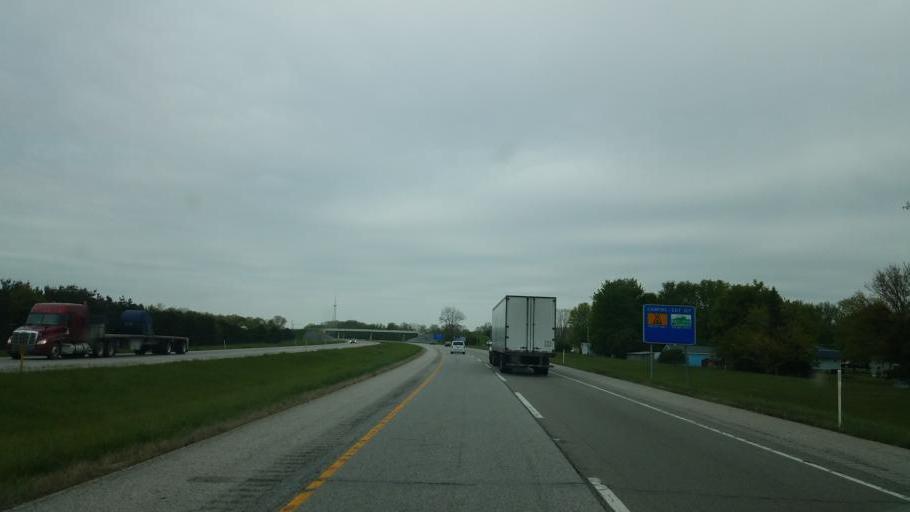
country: US
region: Michigan
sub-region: Saint Joseph County
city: White Pigeon
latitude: 41.7542
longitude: -85.6451
